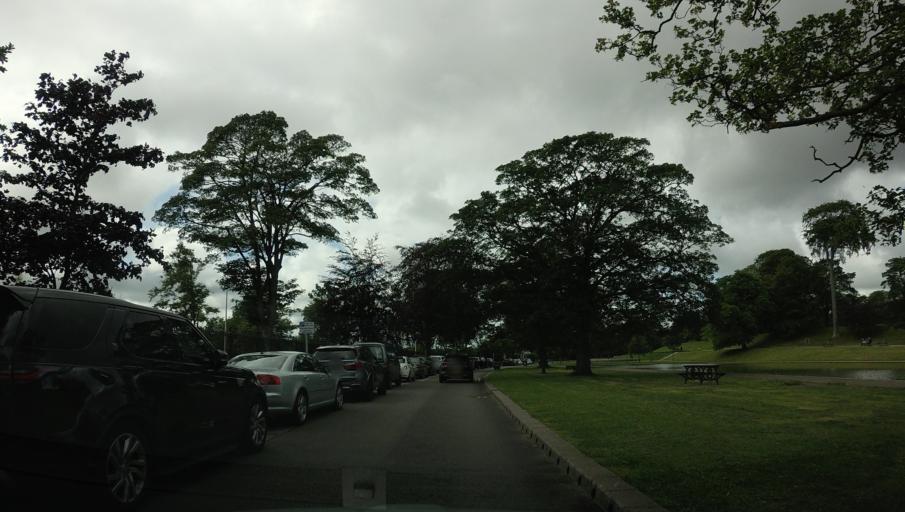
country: GB
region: Scotland
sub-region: Aberdeen City
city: Aberdeen
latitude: 57.1291
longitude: -2.1006
